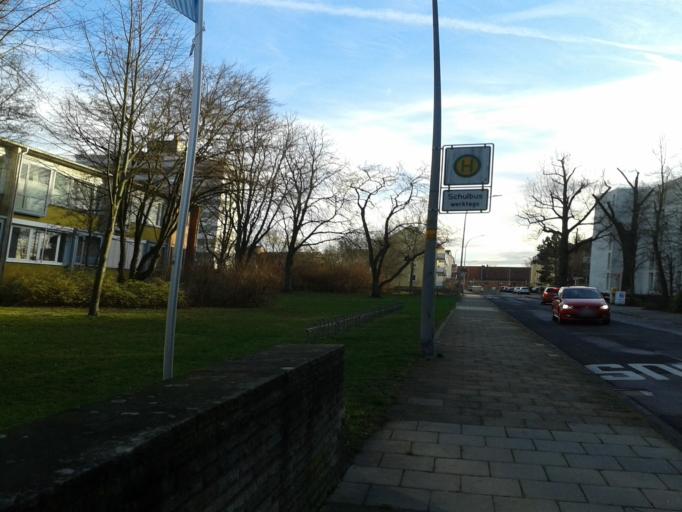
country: DE
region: Bavaria
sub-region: Upper Franconia
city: Bamberg
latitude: 49.9096
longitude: 10.9166
